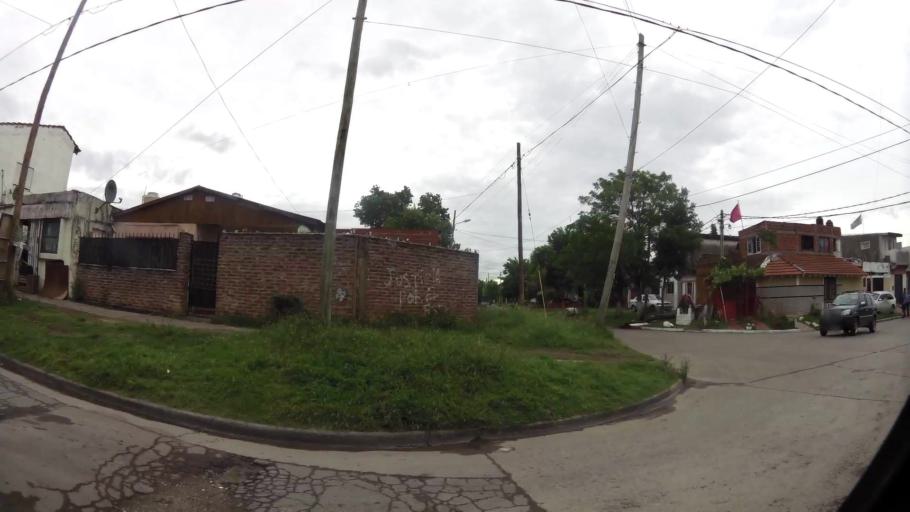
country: AR
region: Buenos Aires
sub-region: Partido de Lanus
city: Lanus
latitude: -34.7364
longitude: -58.3604
